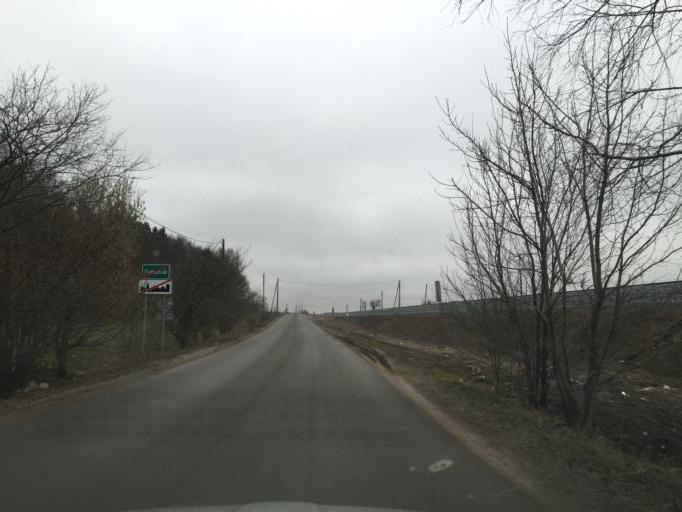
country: PL
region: Pomeranian Voivodeship
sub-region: Powiat kartuski
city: Banino
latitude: 54.4078
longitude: 18.4421
